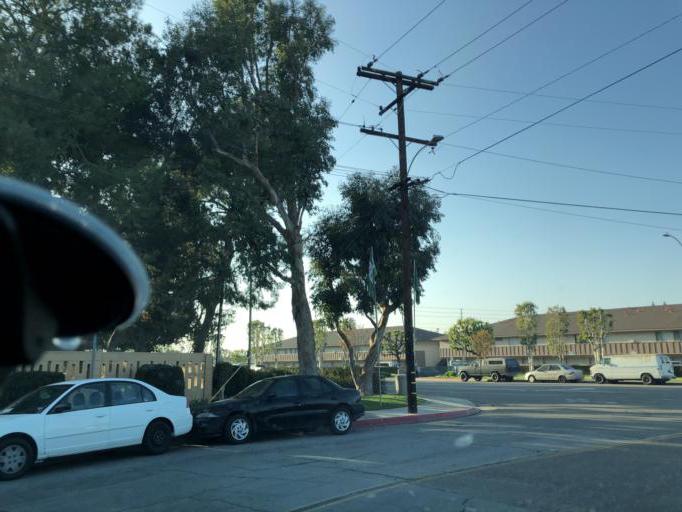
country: US
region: California
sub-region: Orange County
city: Orange
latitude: 33.7801
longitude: -117.8334
